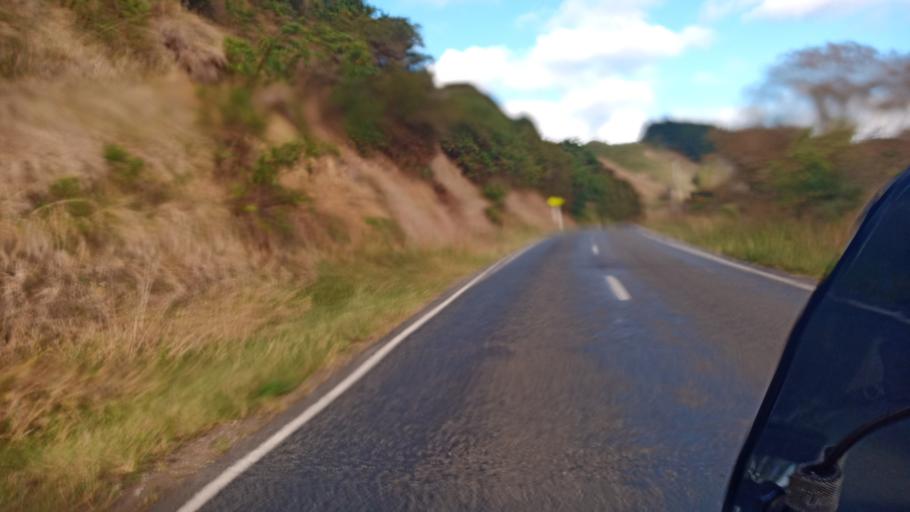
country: NZ
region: Gisborne
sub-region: Gisborne District
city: Gisborne
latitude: -38.5396
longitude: 177.5917
